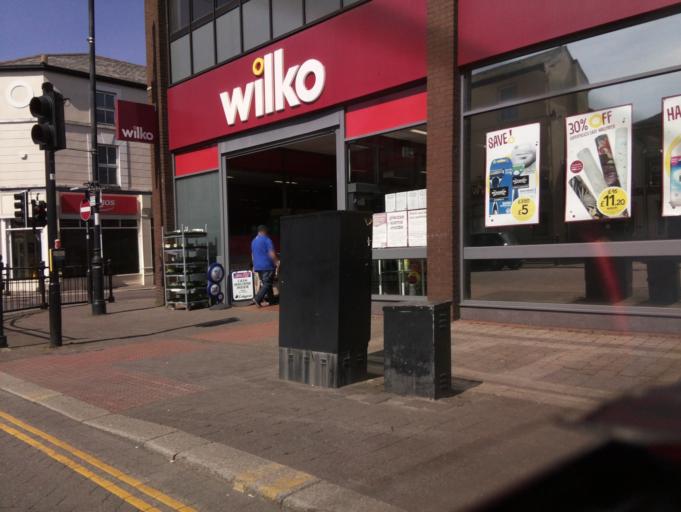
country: GB
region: Wales
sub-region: Rhondda Cynon Taf
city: Aberdare
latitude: 51.7123
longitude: -3.4426
